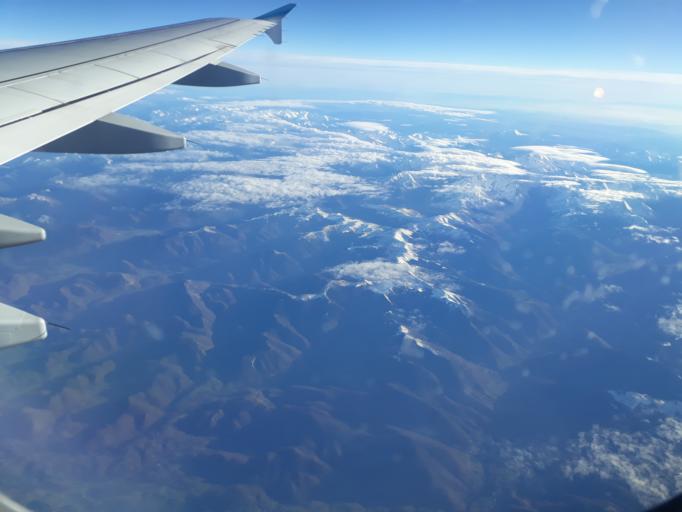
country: FR
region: Midi-Pyrenees
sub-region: Departement des Hautes-Pyrenees
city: Lannemezan
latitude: 43.1260
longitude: 0.3635
